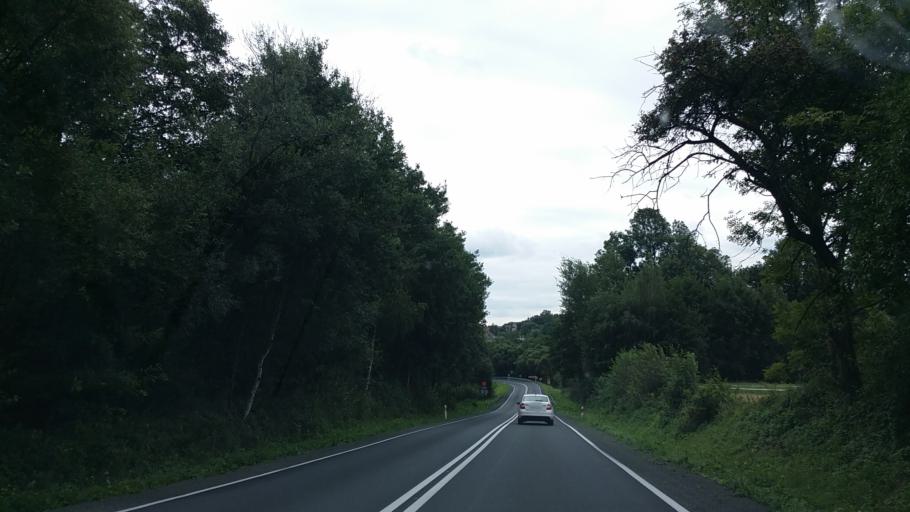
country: PL
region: Lesser Poland Voivodeship
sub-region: Powiat wadowicki
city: Radocza
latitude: 49.9402
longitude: 19.4553
